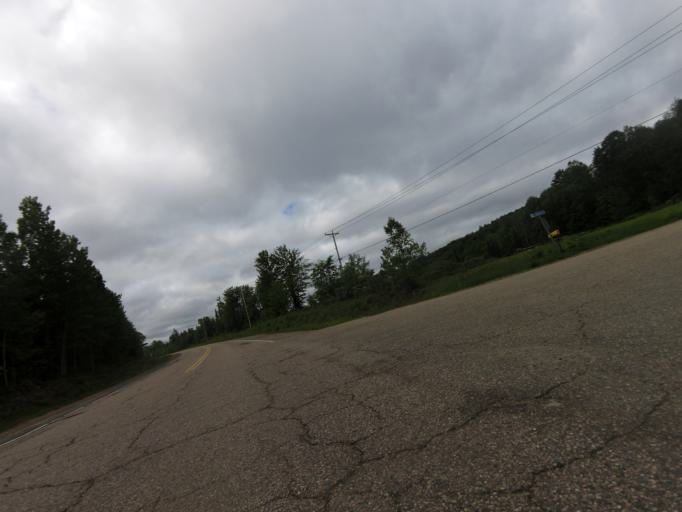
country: CA
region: Quebec
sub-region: Outaouais
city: Shawville
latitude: 45.8261
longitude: -76.4612
